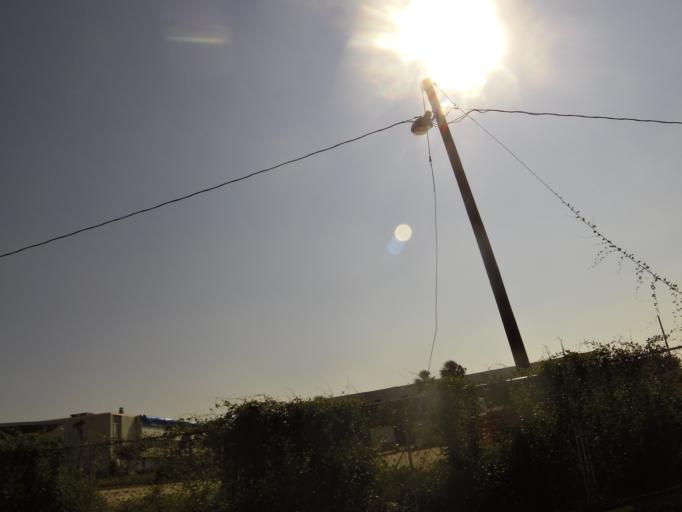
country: US
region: Florida
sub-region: Bay County
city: Panama City
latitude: 30.1541
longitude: -85.6639
